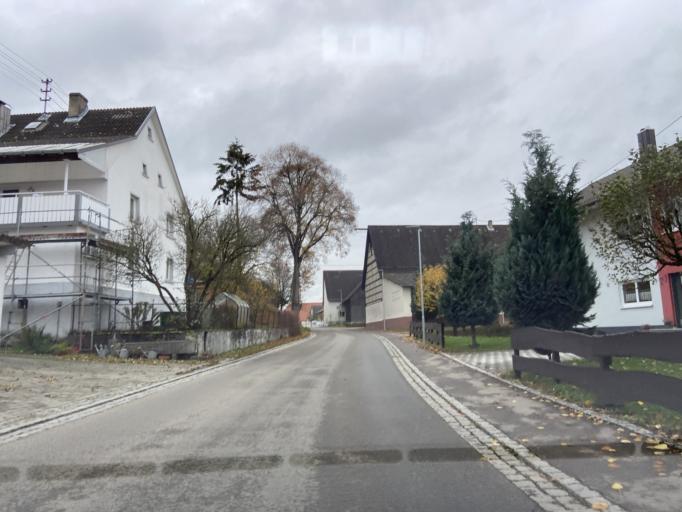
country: DE
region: Baden-Wuerttemberg
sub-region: Tuebingen Region
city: Messkirch
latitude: 48.0104
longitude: 9.1587
